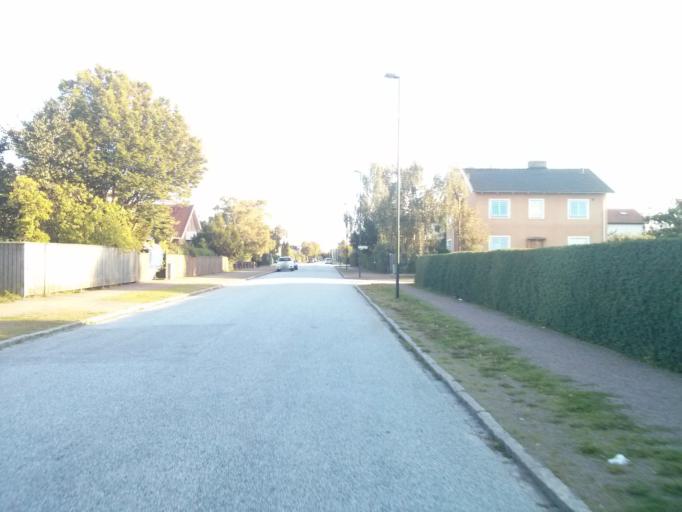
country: SE
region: Skane
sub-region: Malmo
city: Bunkeflostrand
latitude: 55.5803
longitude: 12.9588
